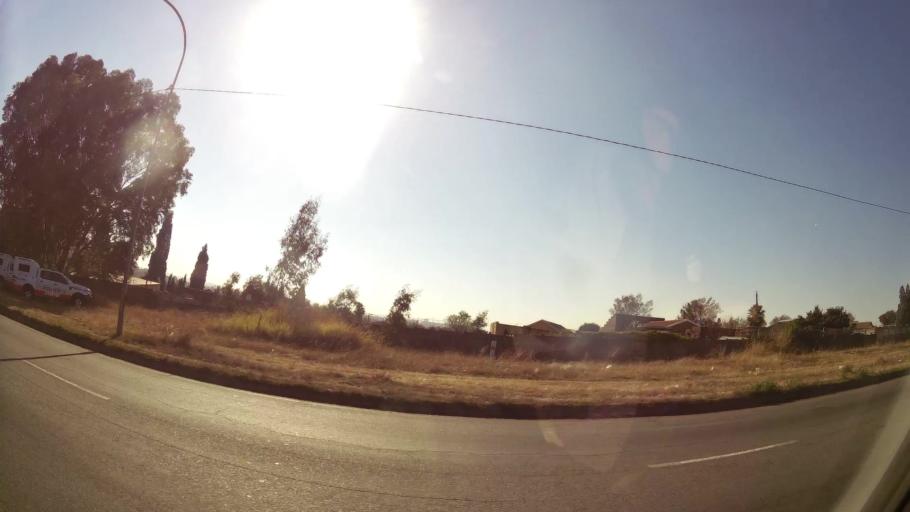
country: ZA
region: Gauteng
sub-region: City of Johannesburg Metropolitan Municipality
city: Johannesburg
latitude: -26.2396
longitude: 28.0998
